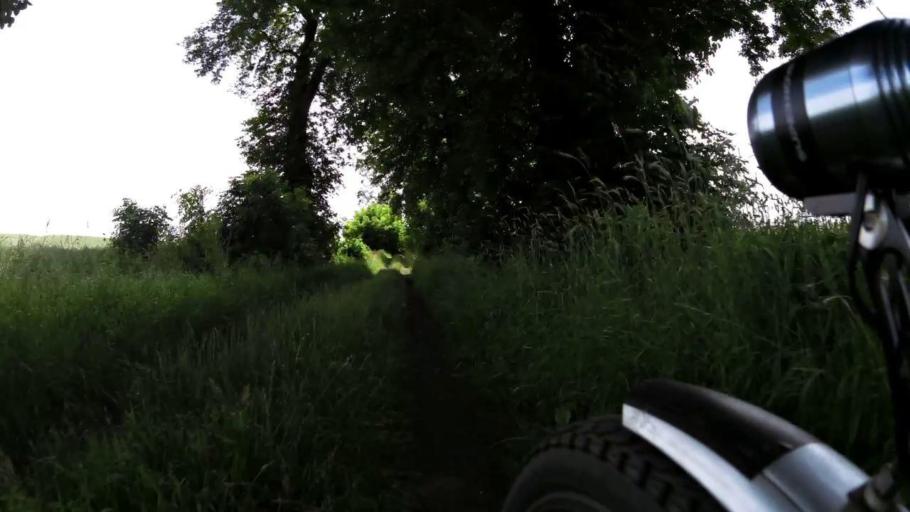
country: PL
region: West Pomeranian Voivodeship
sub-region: Powiat choszczenski
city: Choszczno
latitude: 53.2092
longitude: 15.4396
